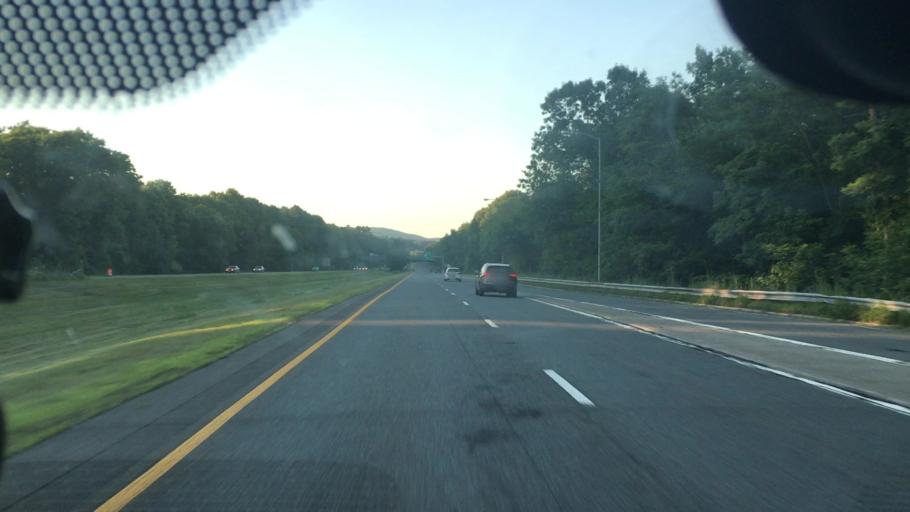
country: US
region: Massachusetts
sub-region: Franklin County
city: Greenfield
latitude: 42.5881
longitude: -72.6203
